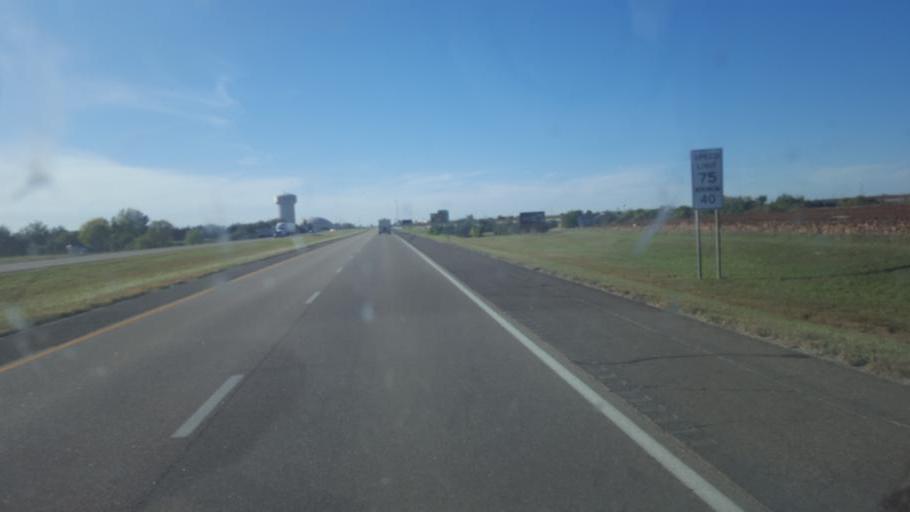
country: US
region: Kansas
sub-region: Ellis County
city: Hays
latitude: 38.8863
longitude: -99.2904
